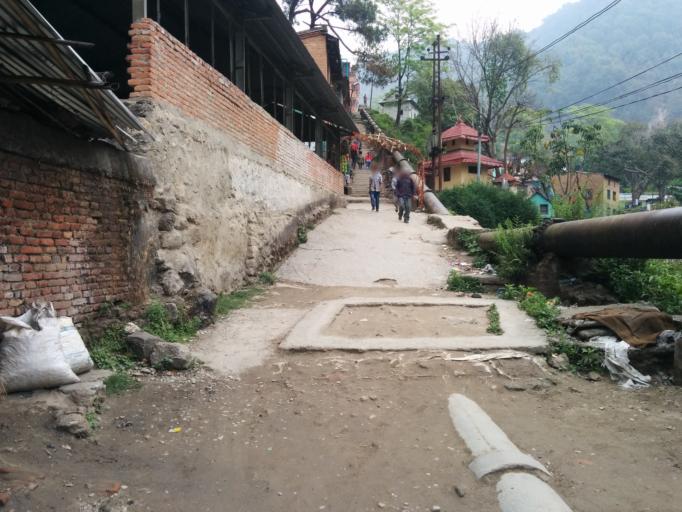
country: NP
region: Central Region
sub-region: Bagmati Zone
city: Bhaktapur
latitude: 27.7613
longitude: 85.4214
